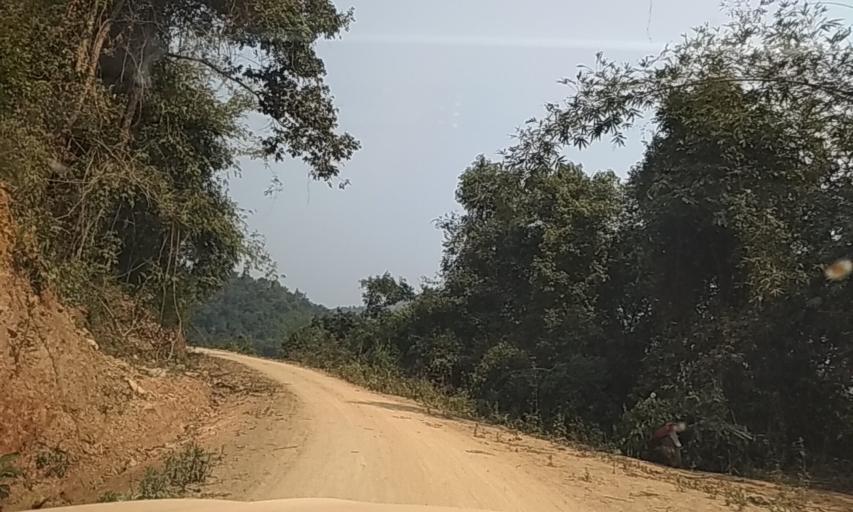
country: LA
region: Phongsali
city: Phongsali
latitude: 21.4707
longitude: 102.4295
